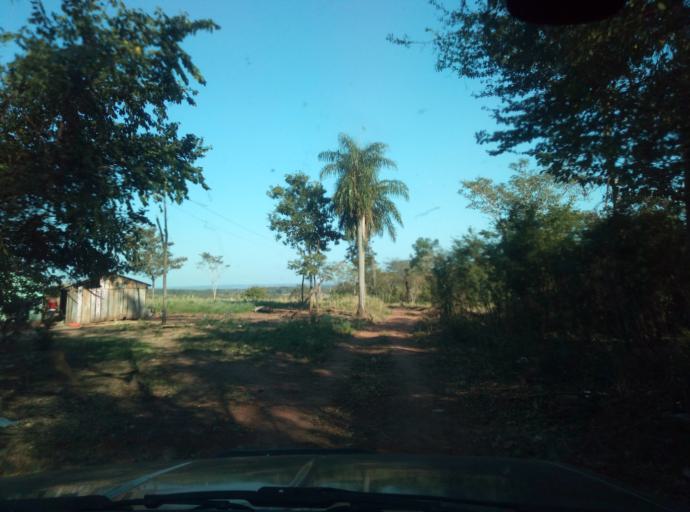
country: PY
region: Caaguazu
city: San Joaquin
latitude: -25.1685
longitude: -56.1147
